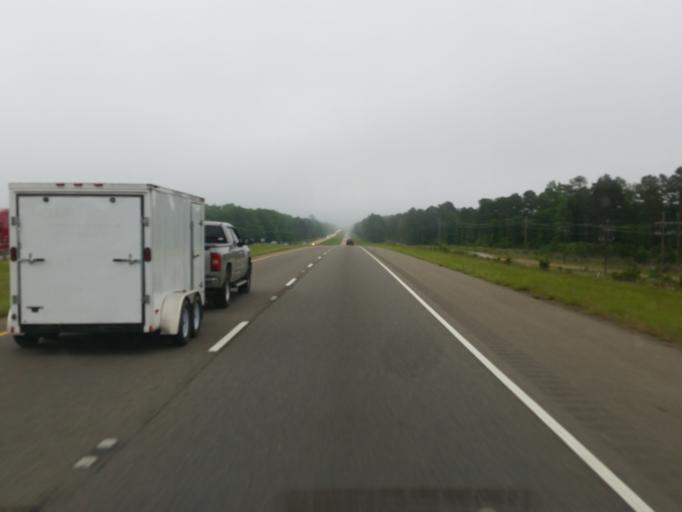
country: US
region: Louisiana
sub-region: Webster Parish
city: Sibley
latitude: 32.5827
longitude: -93.3906
